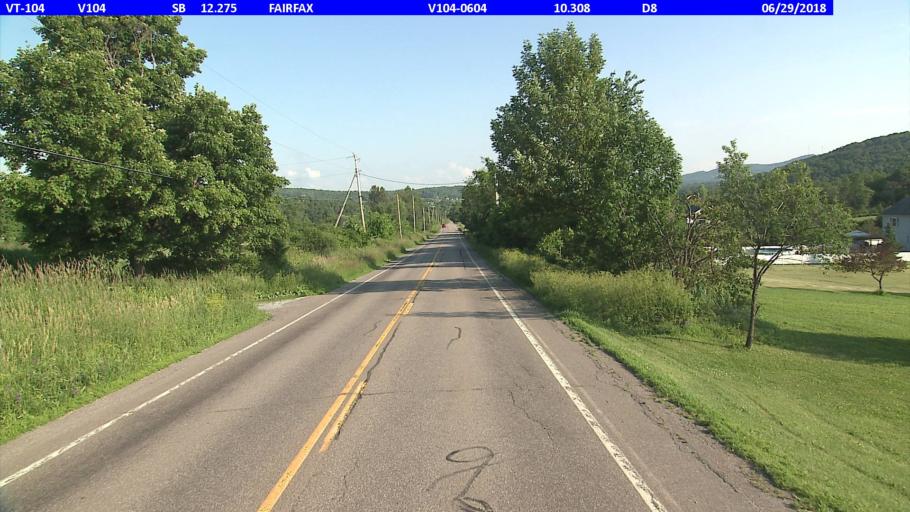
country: US
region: Vermont
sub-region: Franklin County
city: Saint Albans
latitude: 44.7300
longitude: -73.0461
